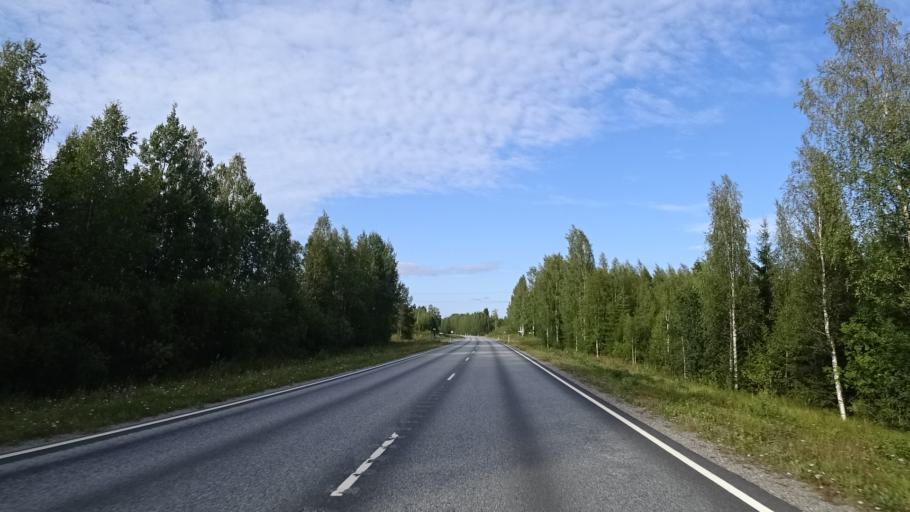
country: FI
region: North Karelia
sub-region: Joensuu
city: Eno
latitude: 62.8170
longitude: 30.1843
